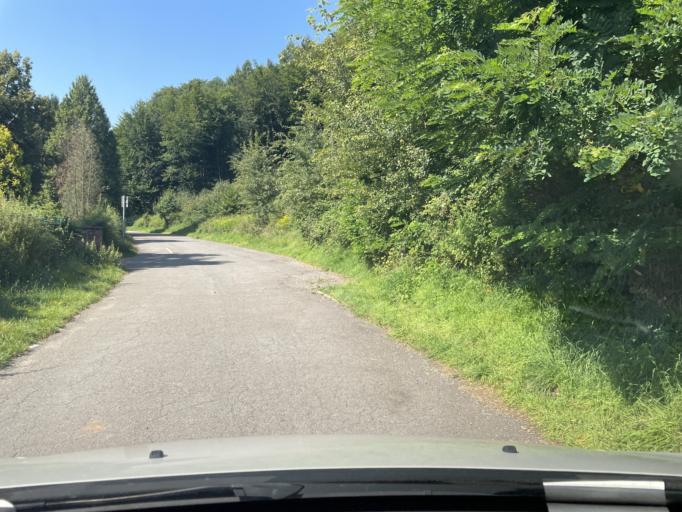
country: DE
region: Saarland
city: Sulzbach
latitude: 49.2543
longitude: 7.0640
